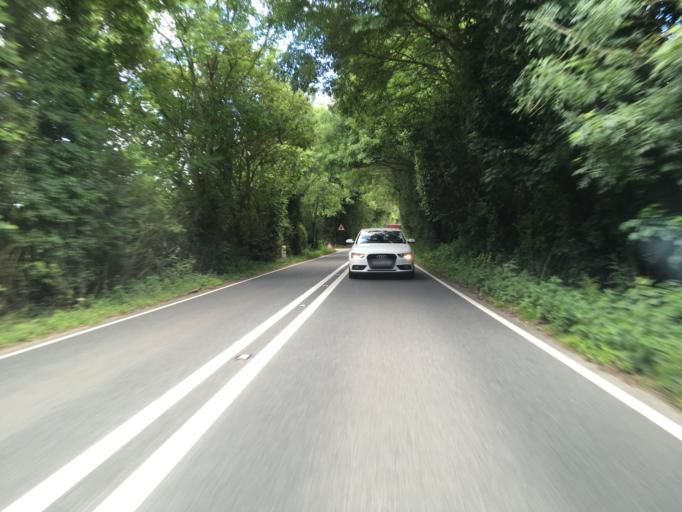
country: GB
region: England
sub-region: Hampshire
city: Highclere
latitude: 51.3338
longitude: -1.3784
